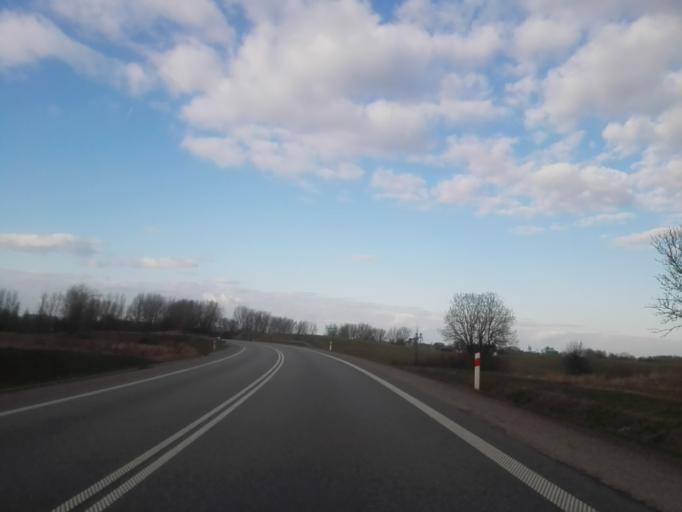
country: PL
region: Podlasie
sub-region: Suwalki
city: Suwalki
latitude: 54.1909
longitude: 23.0102
